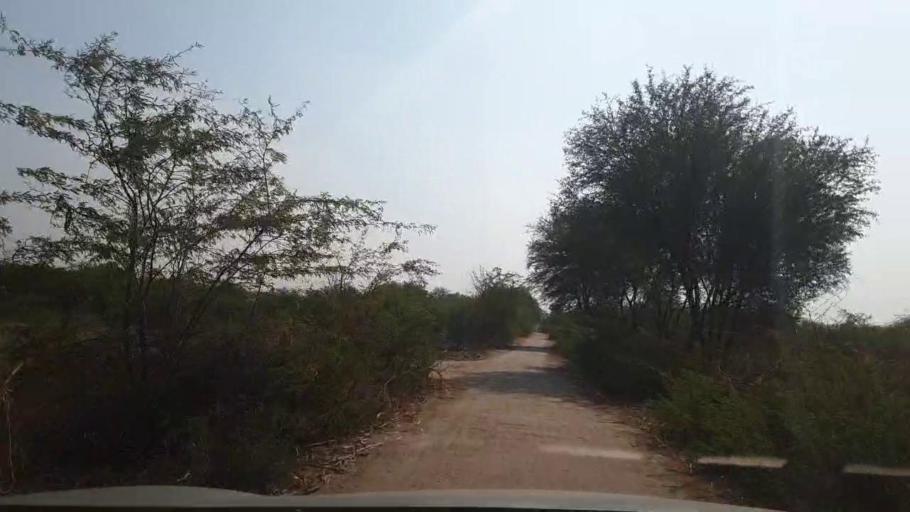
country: PK
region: Sindh
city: Tando Allahyar
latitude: 25.5562
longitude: 68.8476
